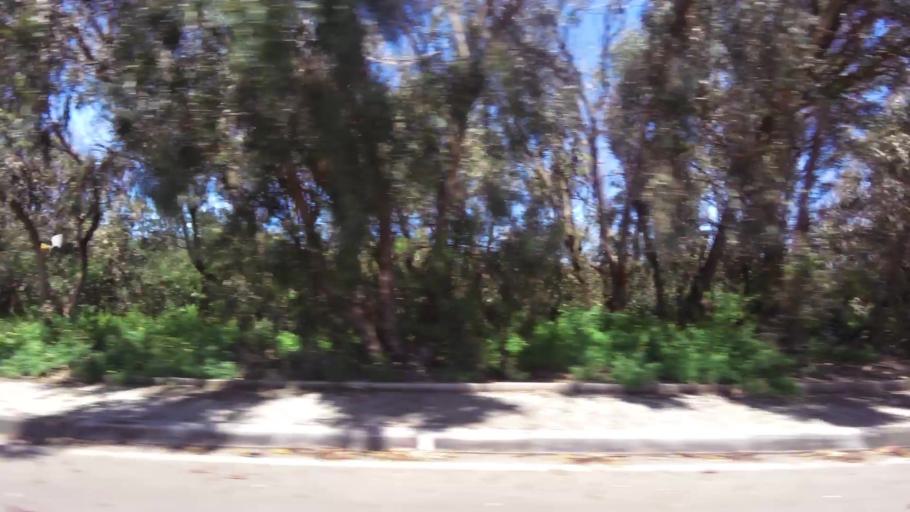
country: MA
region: Grand Casablanca
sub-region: Nouaceur
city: Dar Bouazza
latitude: 33.5352
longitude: -7.7864
